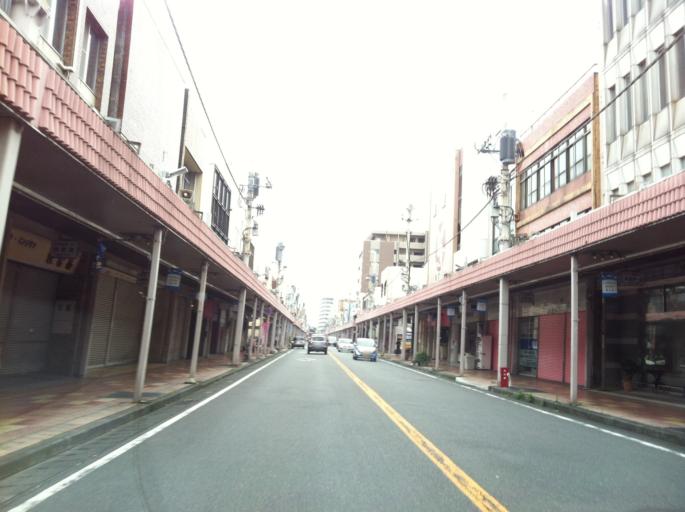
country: JP
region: Shizuoka
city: Fuji
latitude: 35.1561
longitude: 138.6514
